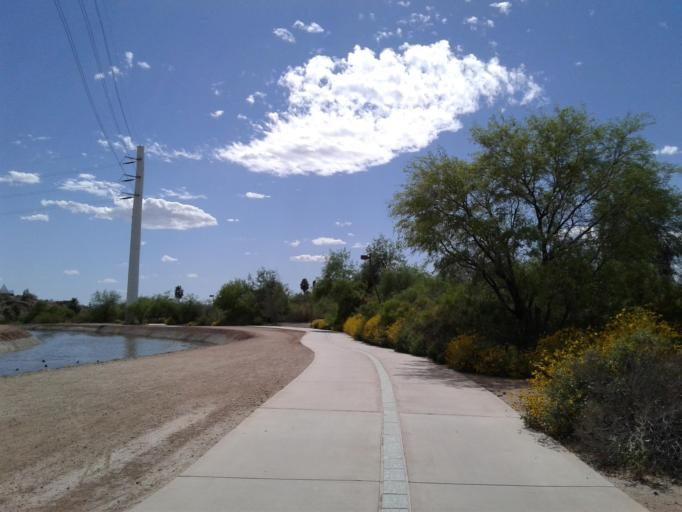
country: US
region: Arizona
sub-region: Maricopa County
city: Tempe Junction
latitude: 33.4585
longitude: -111.9421
